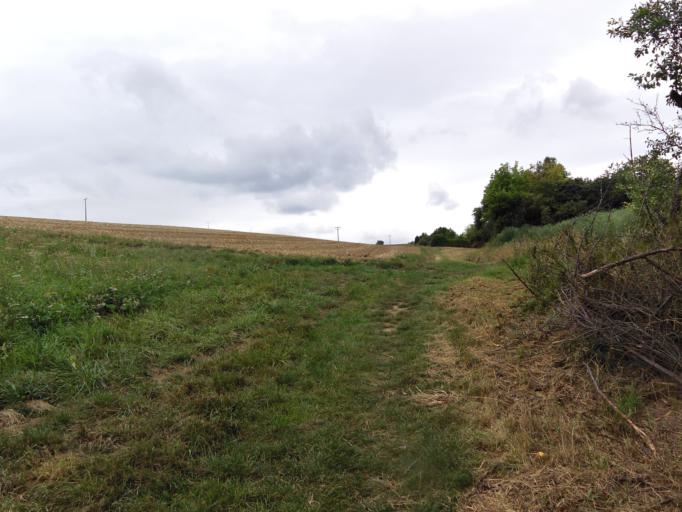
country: DE
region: Bavaria
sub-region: Regierungsbezirk Unterfranken
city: Rimpar
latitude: 49.8570
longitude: 9.9478
